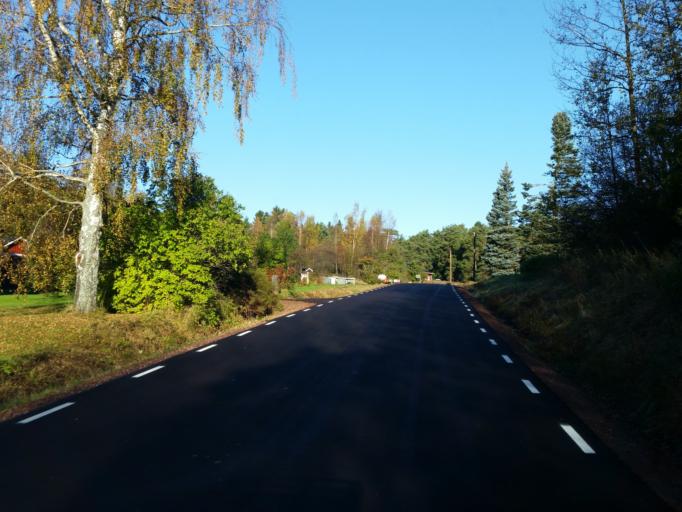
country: AX
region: Alands landsbygd
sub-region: Sund
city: Sund
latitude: 60.2267
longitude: 20.0917
